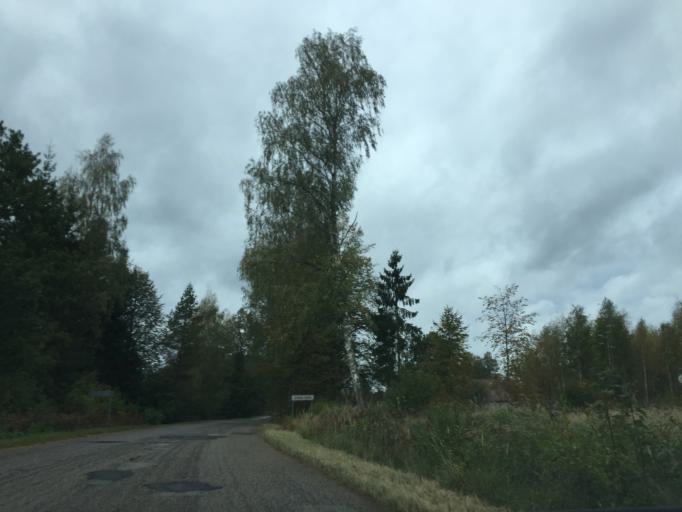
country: LV
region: Olaine
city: Olaine
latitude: 56.7656
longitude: 23.8842
